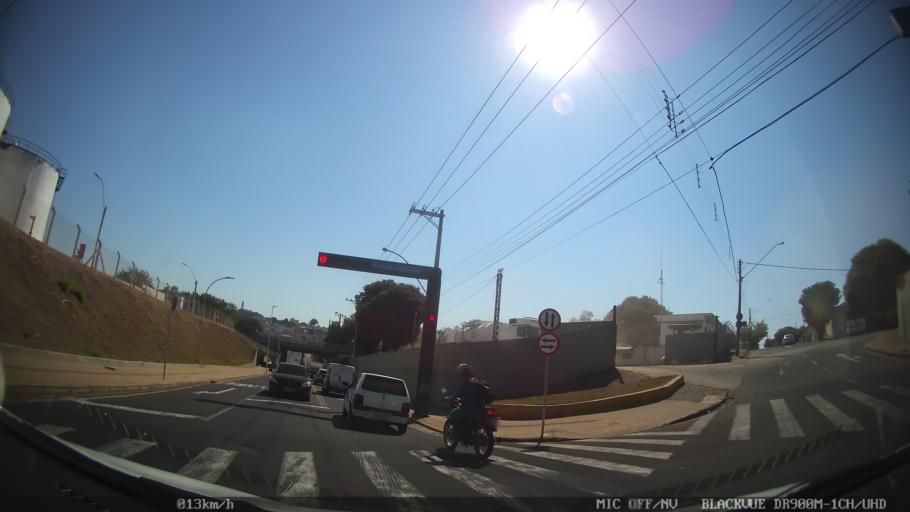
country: BR
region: Sao Paulo
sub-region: Sao Jose Do Rio Preto
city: Sao Jose do Rio Preto
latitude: -20.7921
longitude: -49.3877
